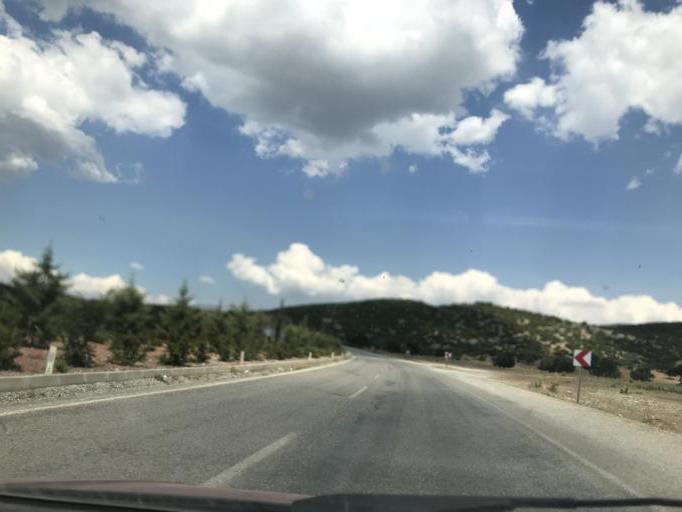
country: TR
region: Denizli
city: Tavas
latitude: 37.5825
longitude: 29.0988
